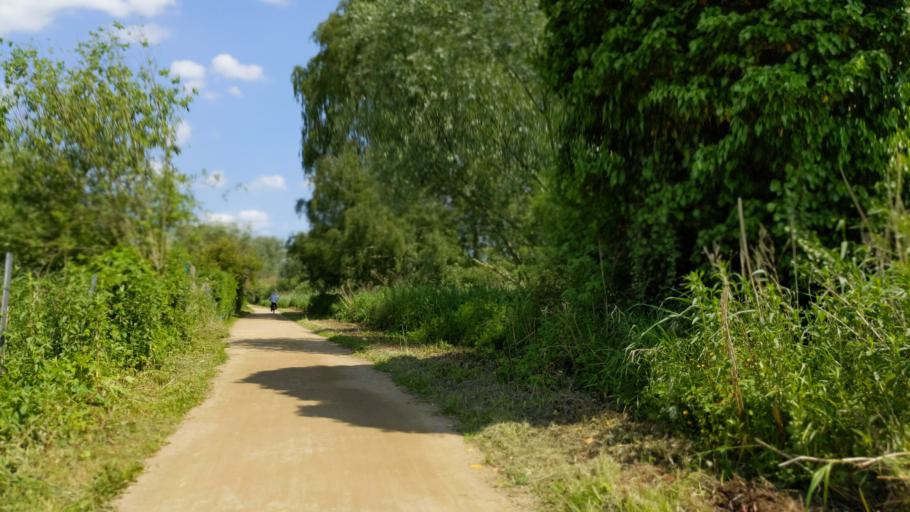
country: DE
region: Schleswig-Holstein
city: Luebeck
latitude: 53.8471
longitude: 10.6635
